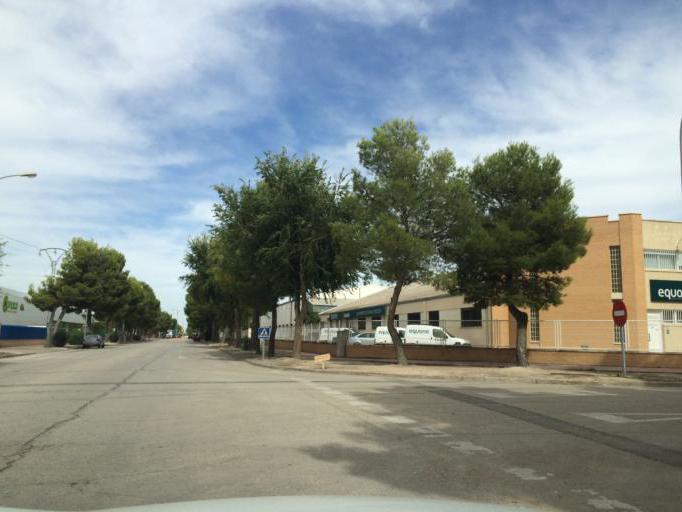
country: ES
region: Castille-La Mancha
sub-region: Provincia de Albacete
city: Albacete
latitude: 39.0120
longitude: -1.8822
